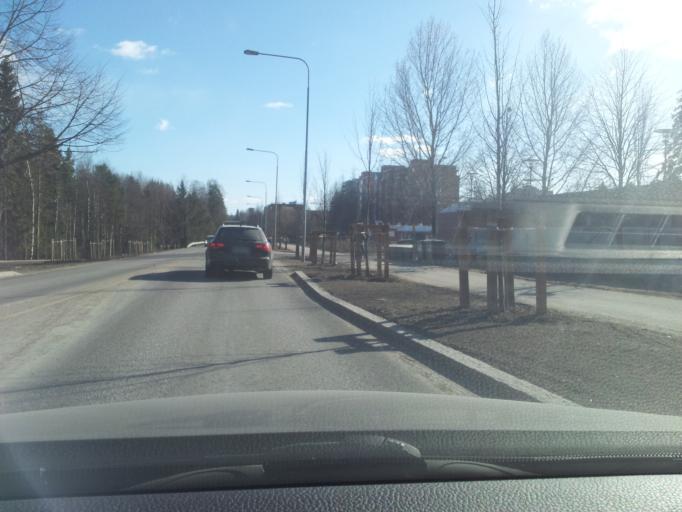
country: FI
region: Uusimaa
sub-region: Helsinki
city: Koukkuniemi
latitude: 60.1710
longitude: 24.7322
